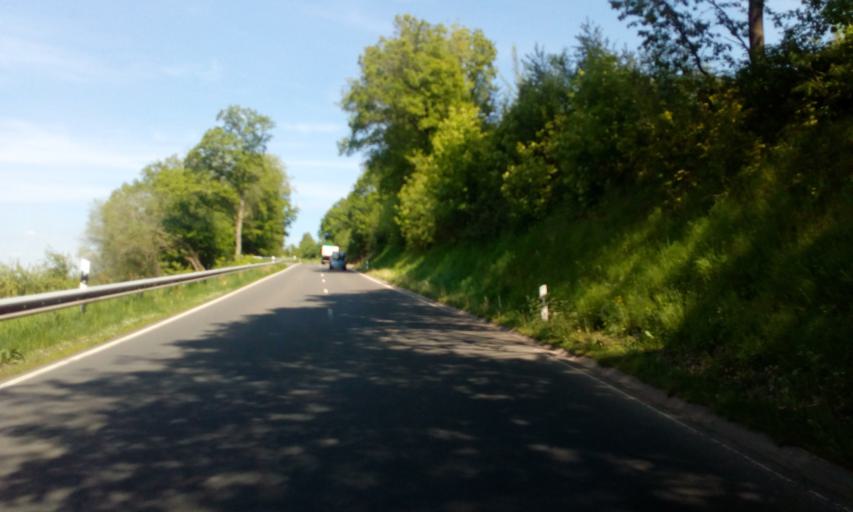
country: DE
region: Rheinland-Pfalz
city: Sinspelt
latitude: 49.9765
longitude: 6.3346
